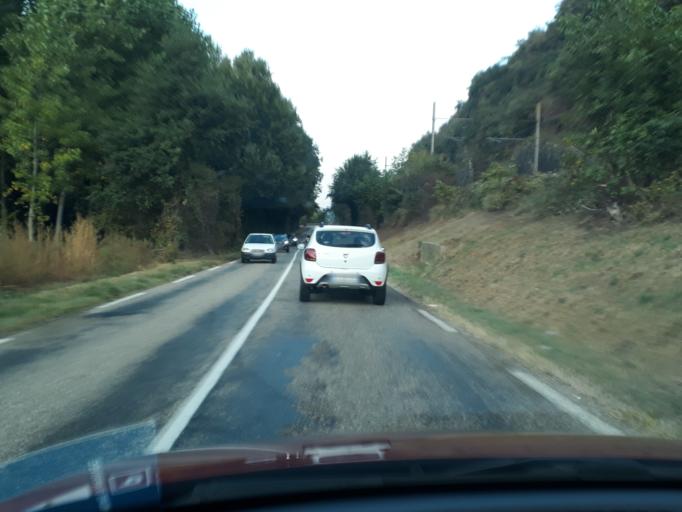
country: FR
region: Rhone-Alpes
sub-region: Departement du Rhone
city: Ampuis
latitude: 45.4756
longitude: 4.7975
